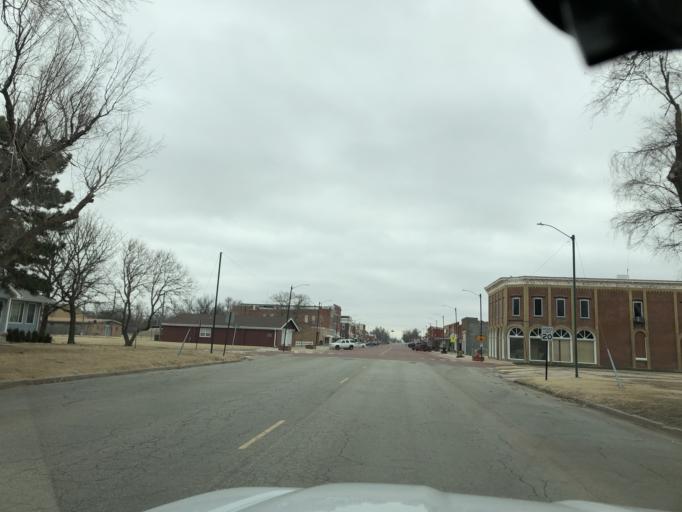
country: US
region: Kansas
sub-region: Stafford County
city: Stafford
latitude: 37.9639
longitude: -98.6005
